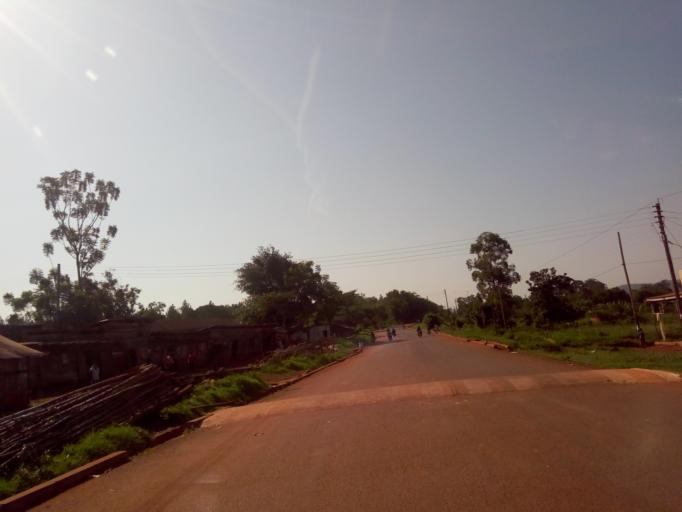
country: UG
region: Western Region
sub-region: Masindi District
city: Masindi
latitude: 1.6939
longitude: 31.7116
